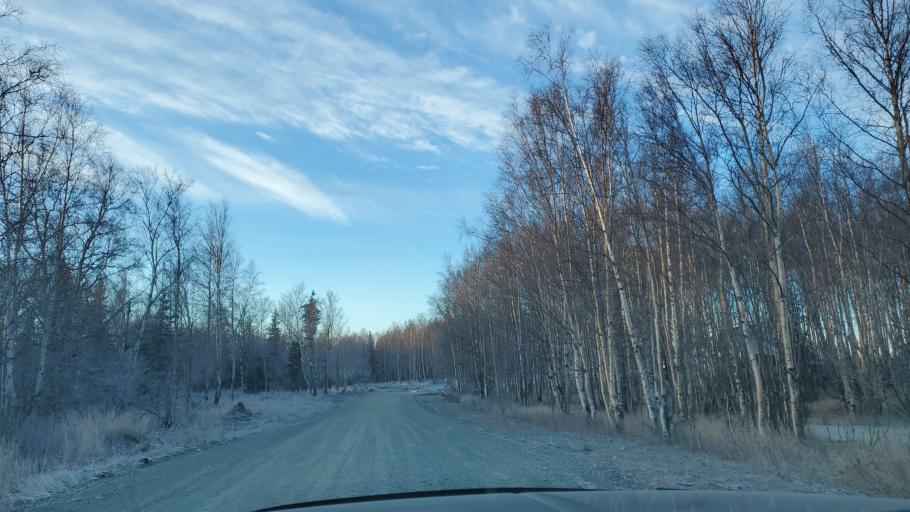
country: US
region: Alaska
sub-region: Matanuska-Susitna Borough
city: Wasilla
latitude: 61.5767
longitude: -149.4214
